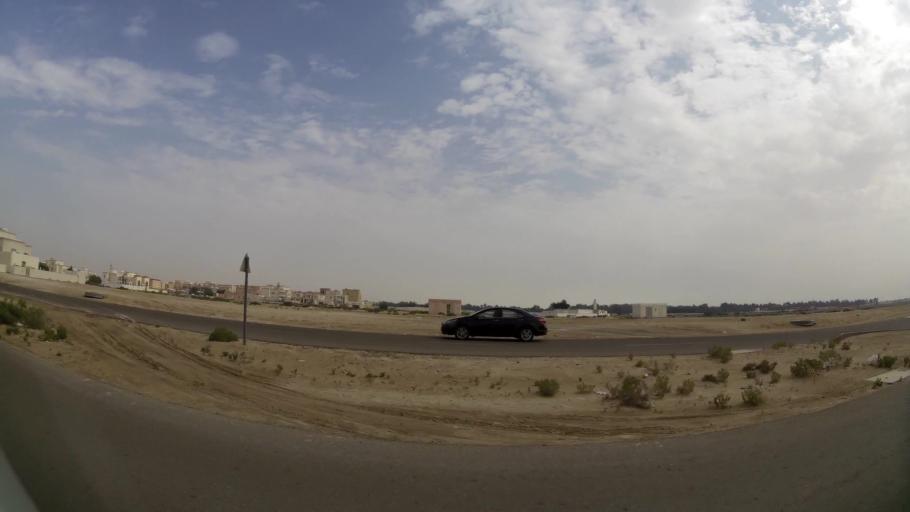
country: AE
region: Abu Dhabi
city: Abu Dhabi
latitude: 24.3043
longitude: 54.6579
